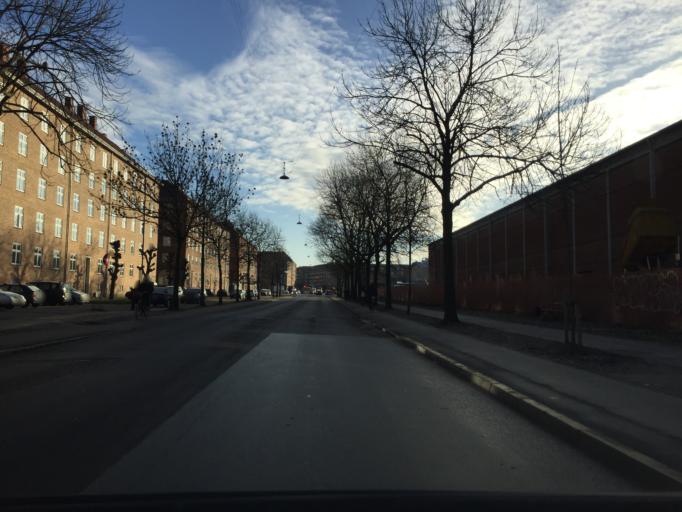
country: DK
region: Capital Region
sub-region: Frederiksberg Kommune
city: Frederiksberg
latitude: 55.6612
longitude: 12.5092
